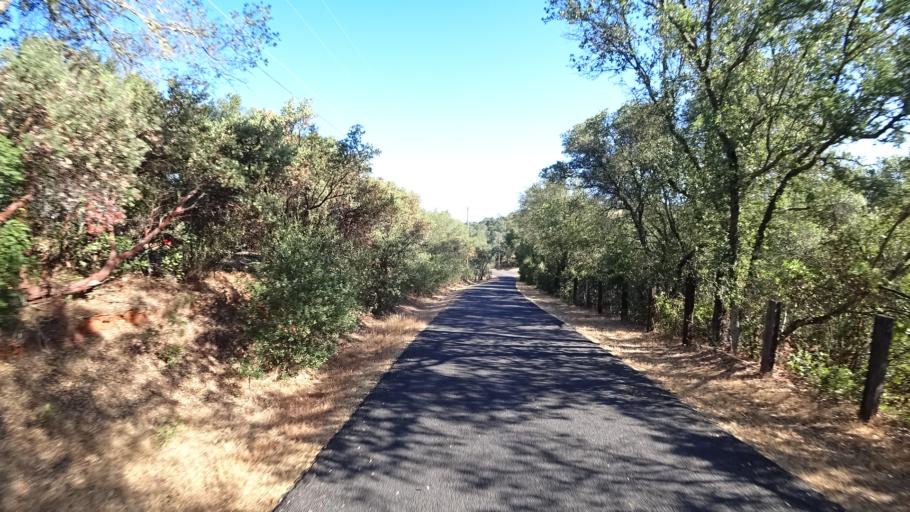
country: US
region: California
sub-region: Calaveras County
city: San Andreas
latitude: 38.2362
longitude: -120.7151
